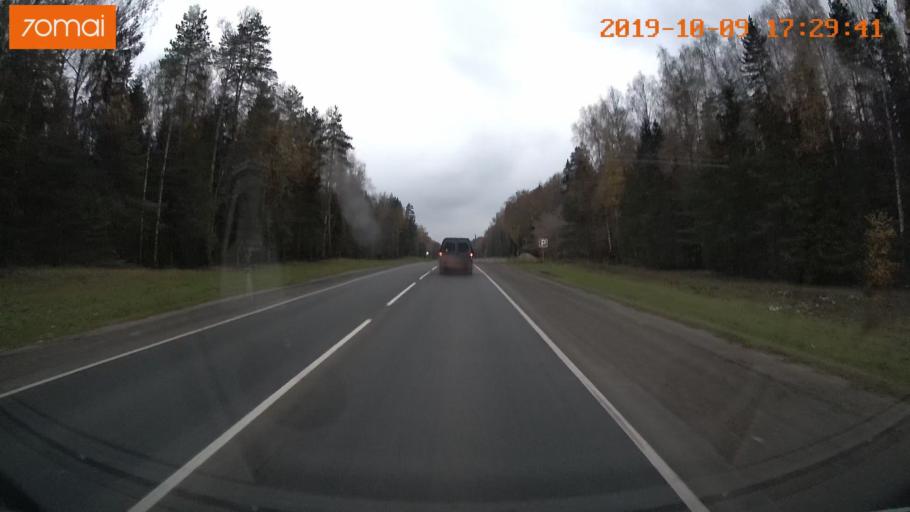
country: RU
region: Ivanovo
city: Bogorodskoye
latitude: 57.1482
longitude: 41.0571
